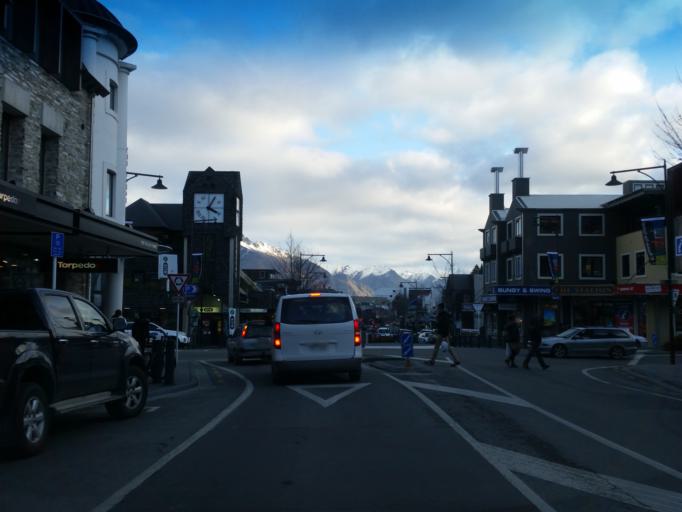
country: NZ
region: Otago
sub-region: Queenstown-Lakes District
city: Queenstown
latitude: -45.0306
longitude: 168.6608
